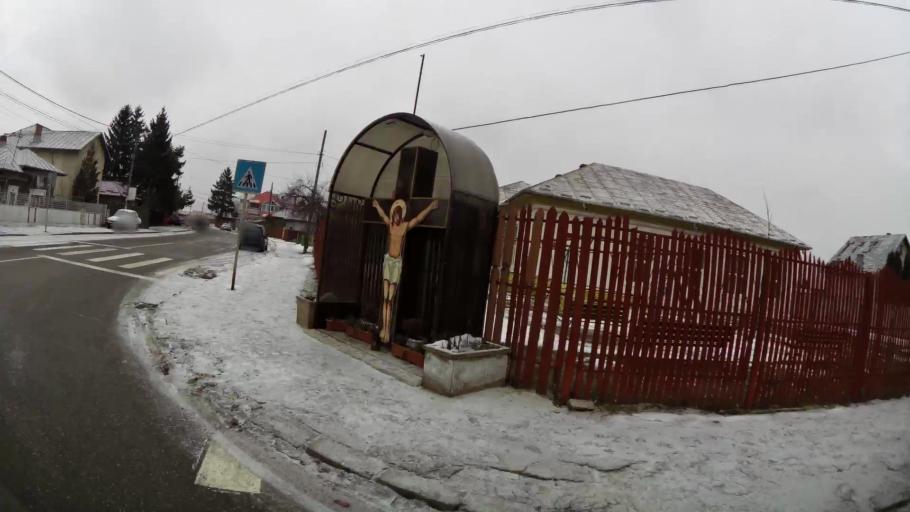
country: RO
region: Dambovita
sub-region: Comuna Ulmi
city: Ulmi
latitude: 44.9167
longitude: 25.4833
